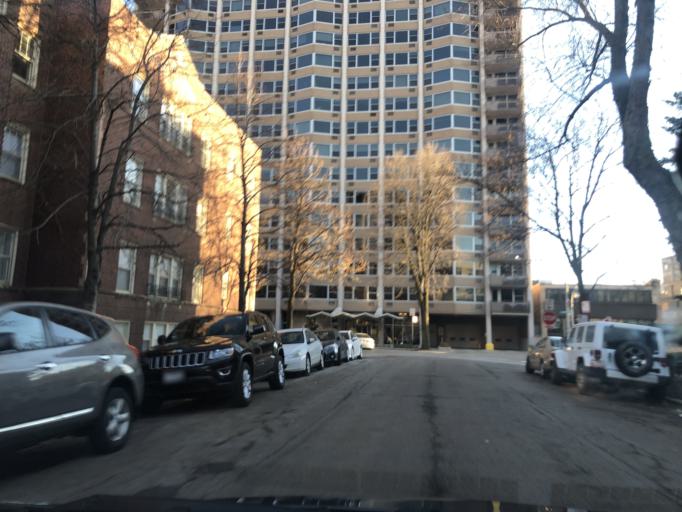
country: US
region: Illinois
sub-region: Cook County
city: Chicago
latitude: 41.9465
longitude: -87.6447
